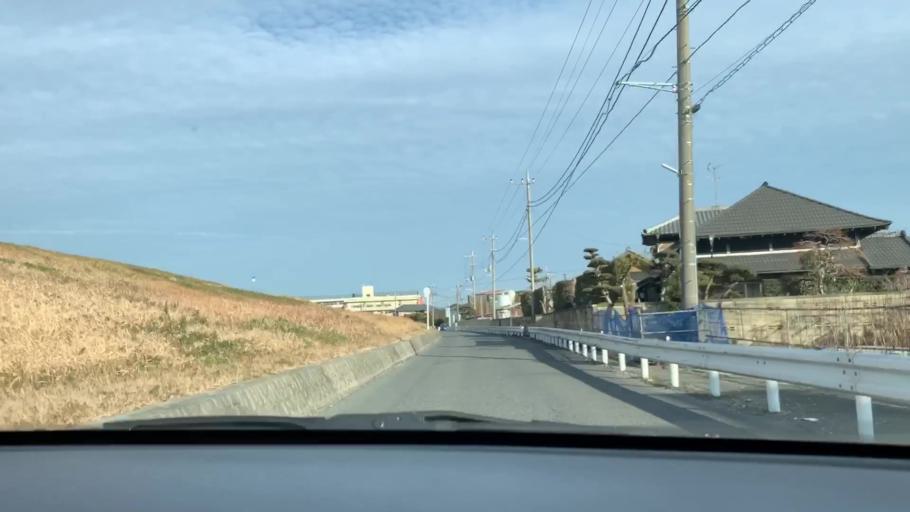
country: JP
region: Chiba
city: Matsudo
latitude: 35.8012
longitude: 139.8946
